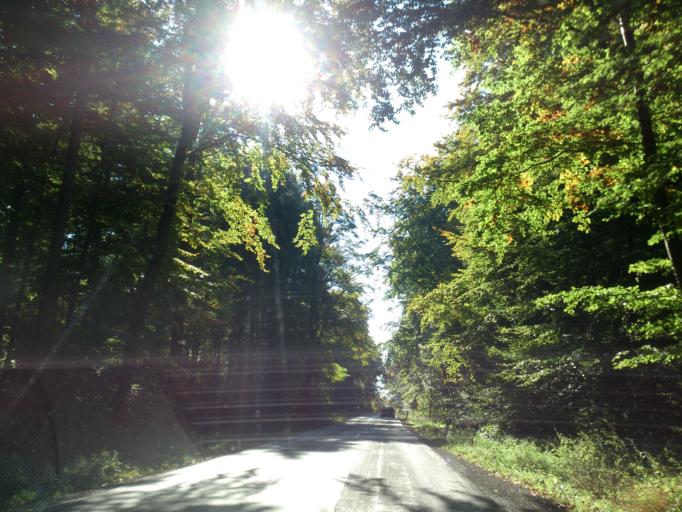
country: DE
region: Hesse
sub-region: Regierungsbezirk Kassel
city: Calden
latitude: 51.3816
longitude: 9.4180
